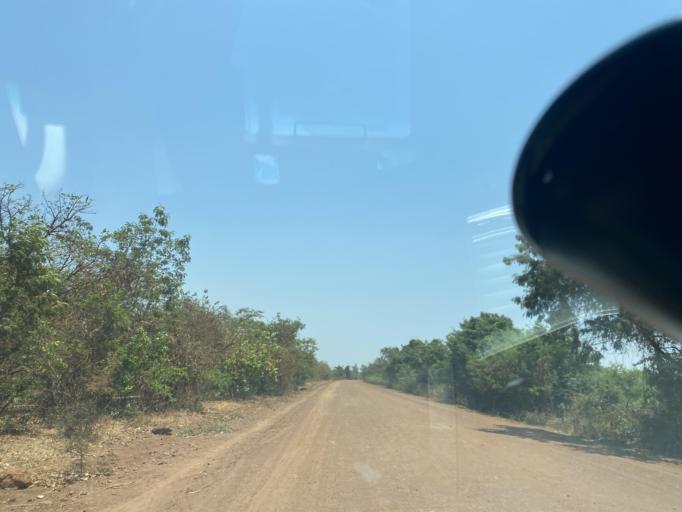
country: ZM
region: Southern
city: Nakambala
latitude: -15.4925
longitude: 27.9043
